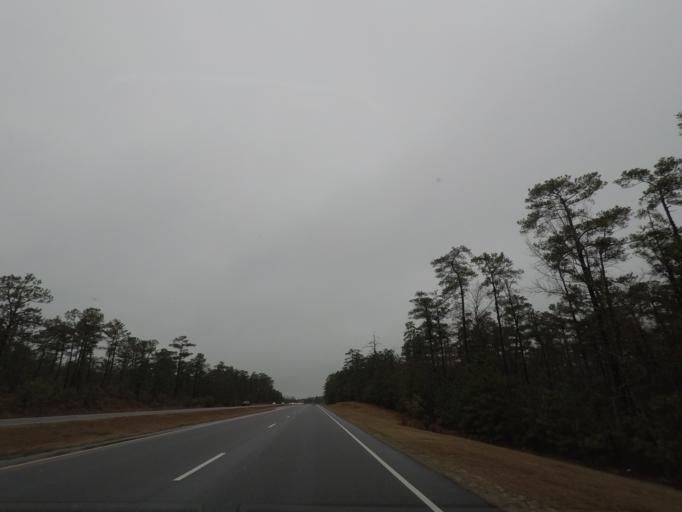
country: US
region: North Carolina
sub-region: Cumberland County
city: Spring Lake
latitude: 35.2389
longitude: -79.0208
